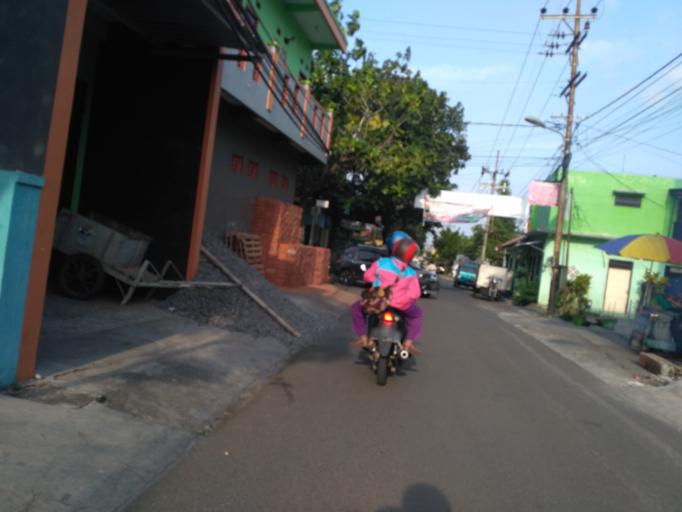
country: ID
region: East Java
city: Malang
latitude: -7.9377
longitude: 112.6304
